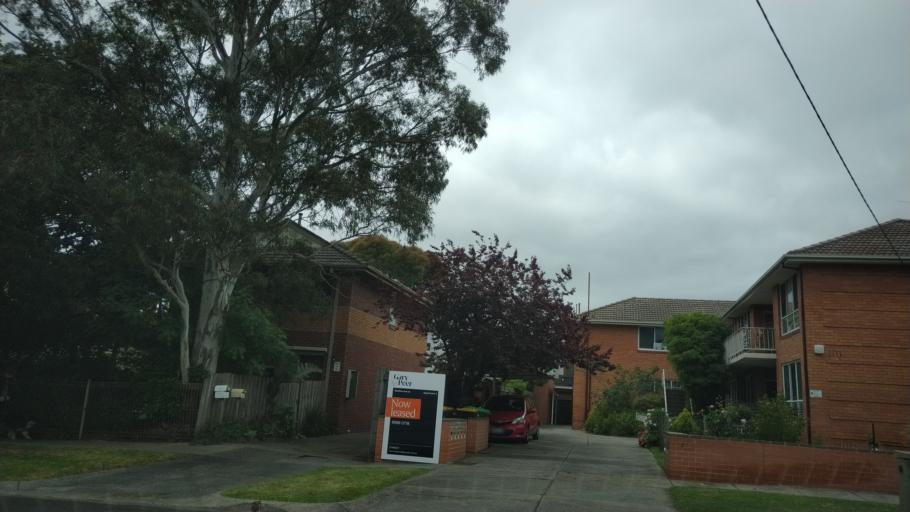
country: AU
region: Victoria
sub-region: Glen Eira
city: Murrumbeena
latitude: -37.8943
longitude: 145.0705
